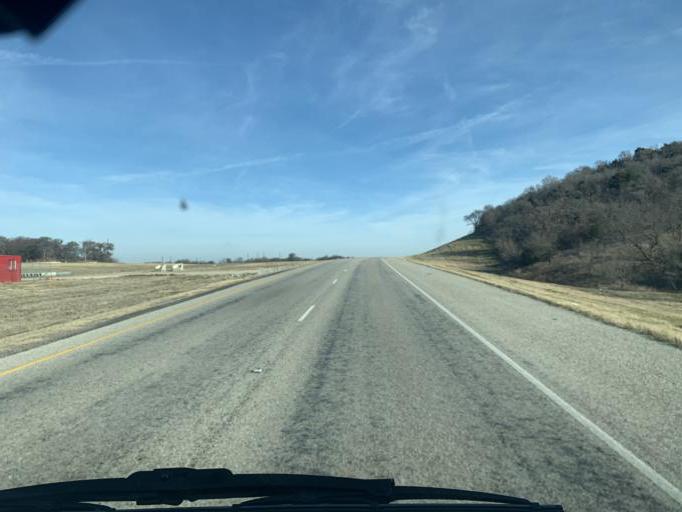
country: US
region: Texas
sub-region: Dallas County
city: Cedar Hill
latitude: 32.6287
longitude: -96.9749
